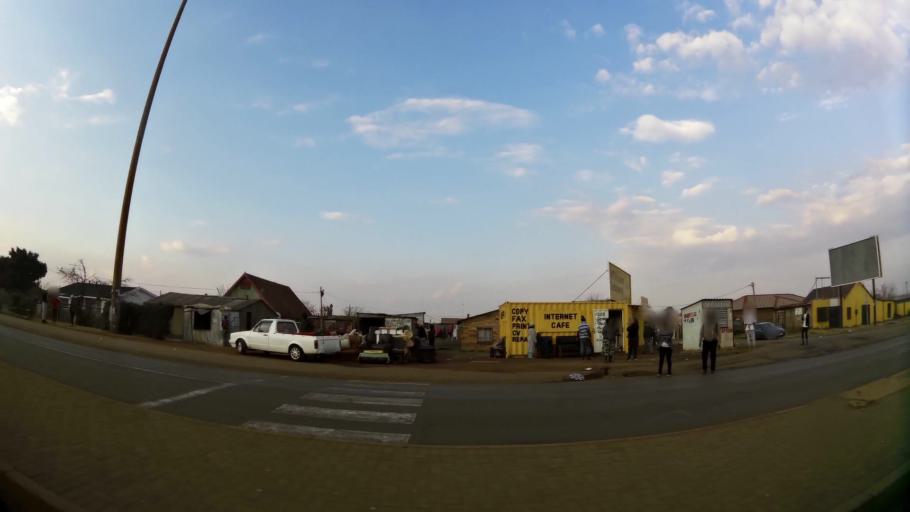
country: ZA
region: Gauteng
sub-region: City of Johannesburg Metropolitan Municipality
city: Orange Farm
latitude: -26.5658
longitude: 27.8349
